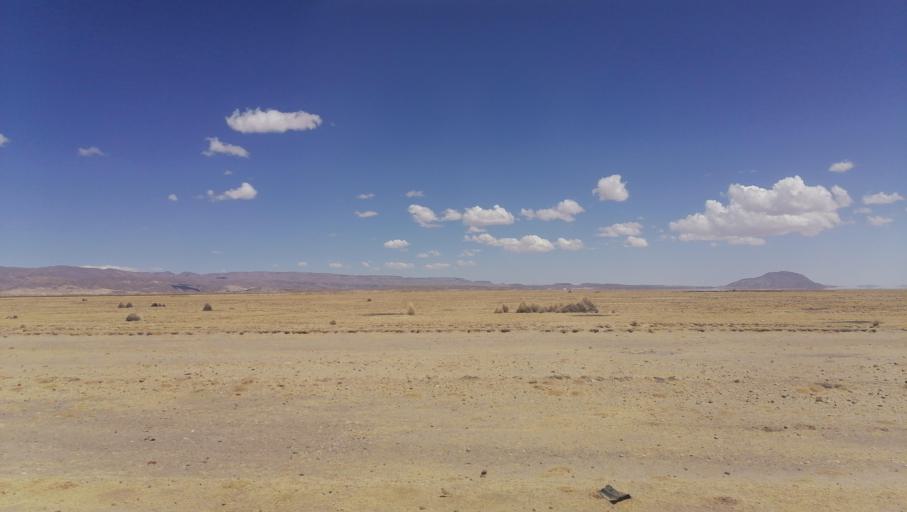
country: BO
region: Oruro
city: Challapata
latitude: -19.1722
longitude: -66.8010
